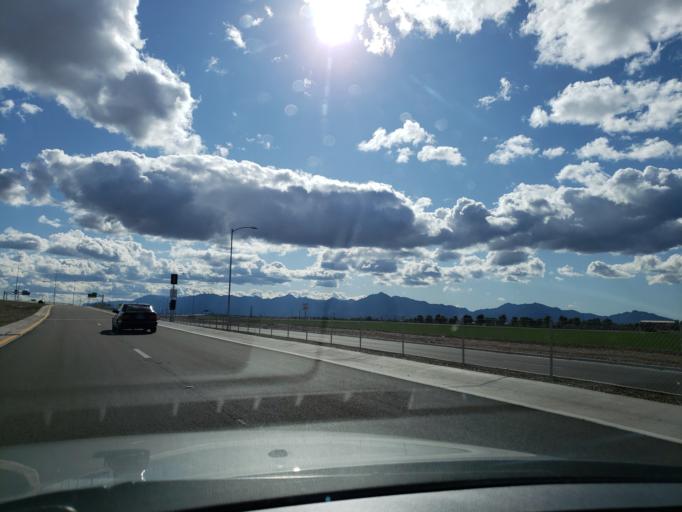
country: US
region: Arizona
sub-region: Maricopa County
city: Tolleson
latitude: 33.4349
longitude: -112.1878
